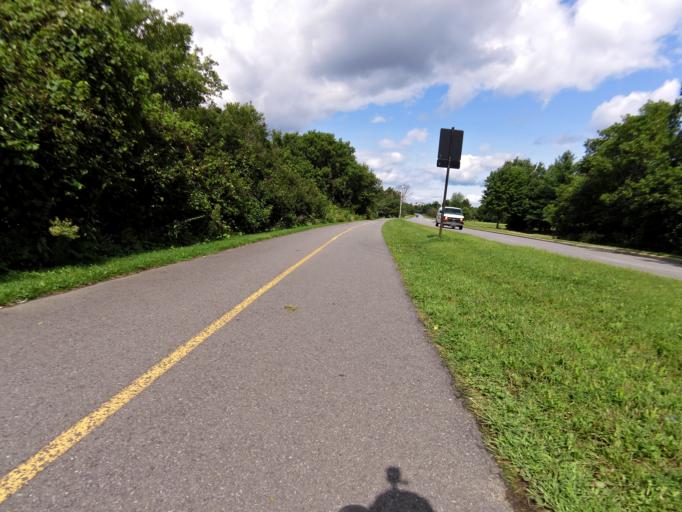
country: CA
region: Ontario
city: Ottawa
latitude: 45.4348
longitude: -75.6348
